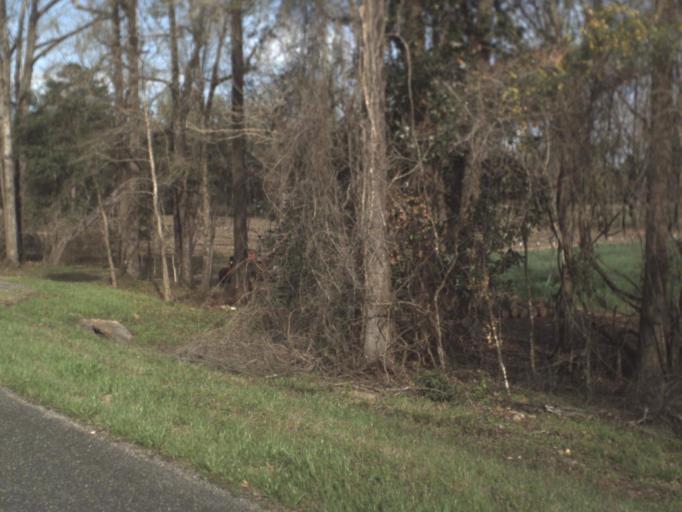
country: US
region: Florida
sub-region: Jefferson County
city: Monticello
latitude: 30.4409
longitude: -83.9036
